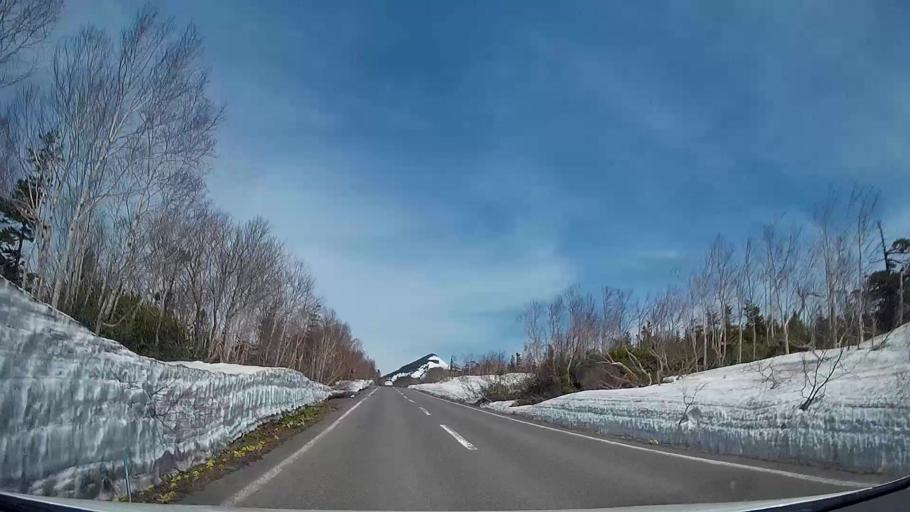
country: JP
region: Iwate
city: Shizukuishi
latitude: 39.9397
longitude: 140.9105
